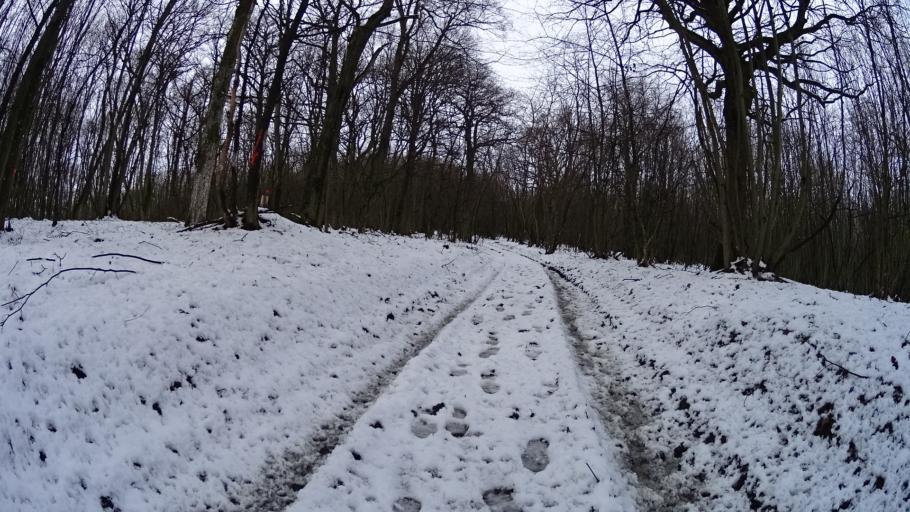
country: AT
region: Lower Austria
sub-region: Politischer Bezirk Korneuburg
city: Niederhollabrunn
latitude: 48.4145
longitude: 16.3018
